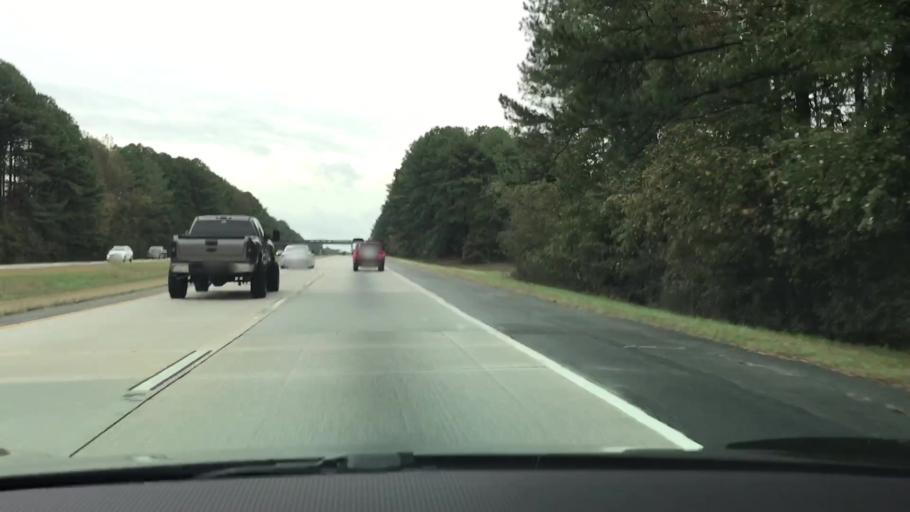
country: US
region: Georgia
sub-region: Greene County
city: Union Point
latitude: 33.5412
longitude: -83.0128
